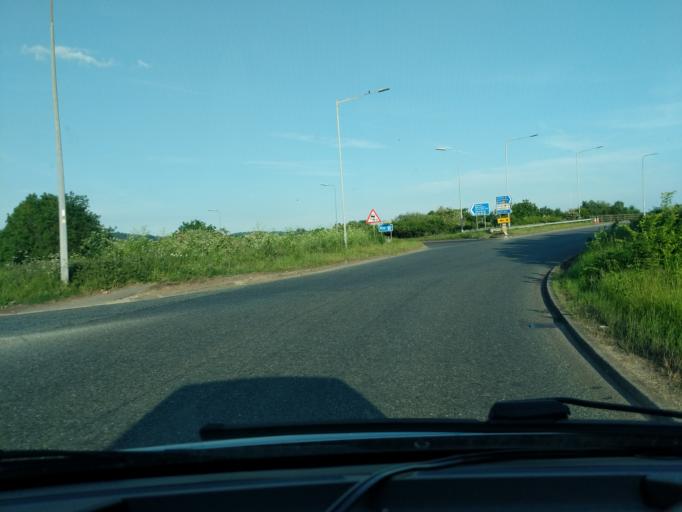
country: GB
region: England
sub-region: Cheshire West and Chester
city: Elton
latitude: 53.2674
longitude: -2.8037
